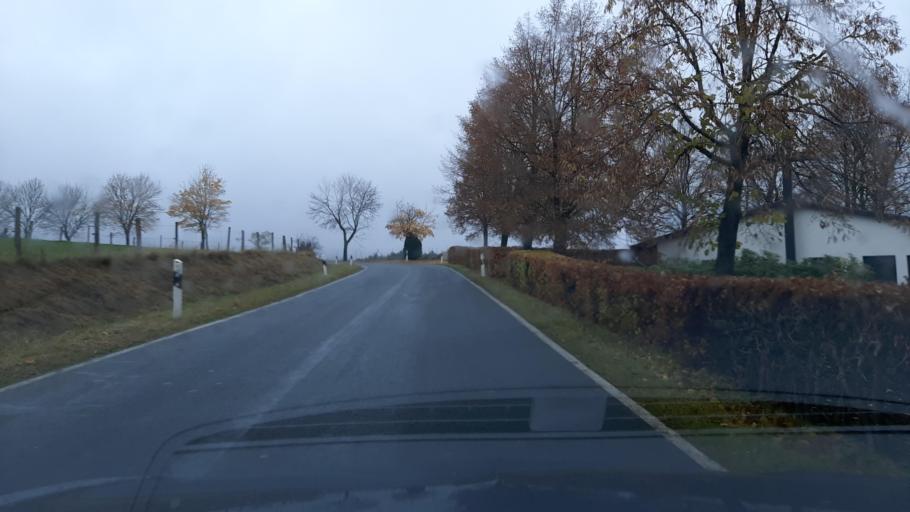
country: DE
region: North Rhine-Westphalia
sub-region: Regierungsbezirk Arnsberg
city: Olsberg
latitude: 51.2921
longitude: 8.4961
